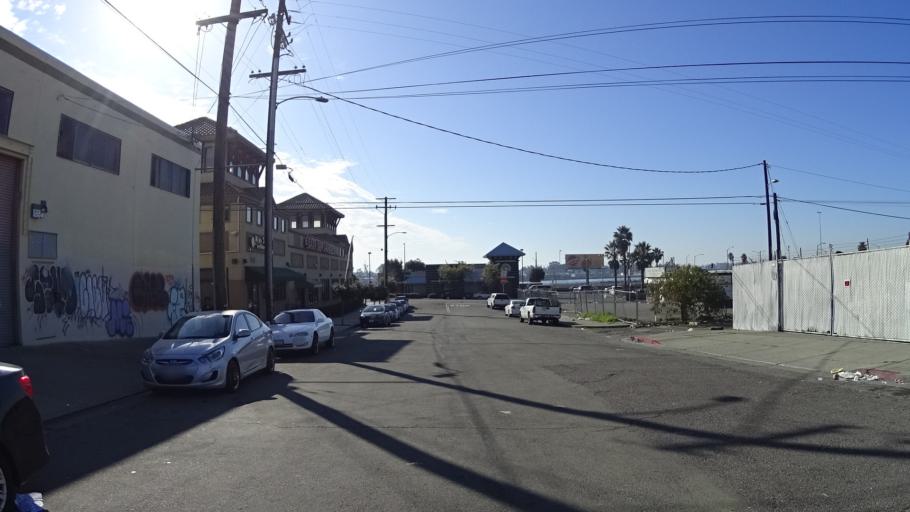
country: US
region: California
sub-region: Alameda County
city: Alameda
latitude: 37.7887
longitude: -122.2455
